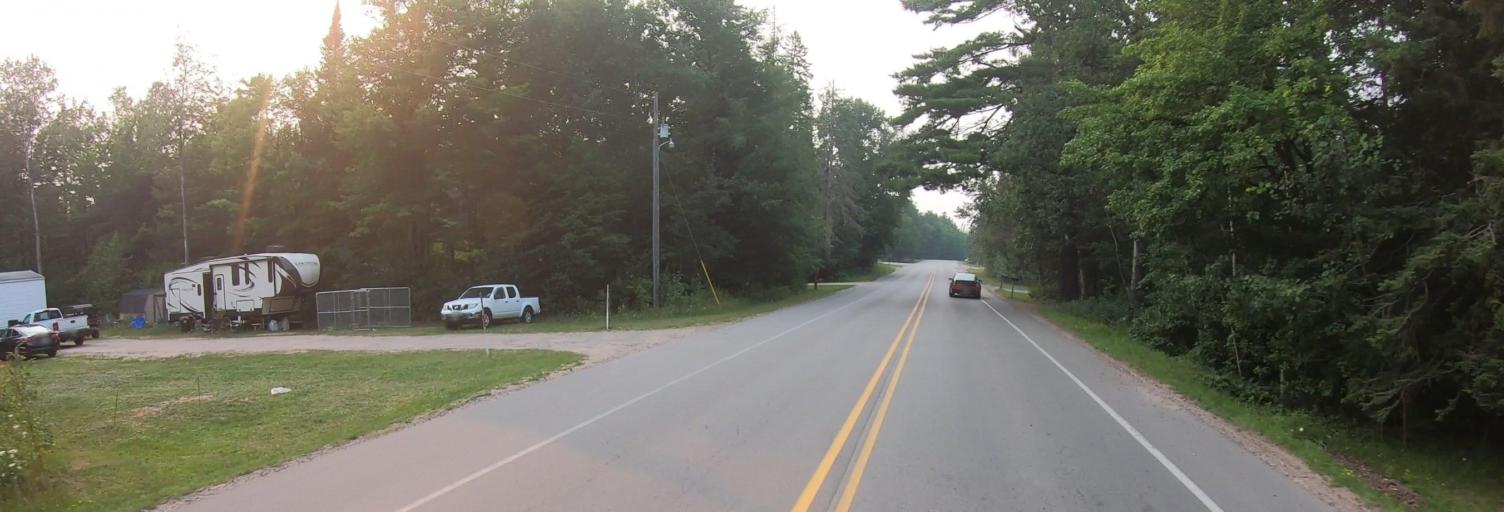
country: US
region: Michigan
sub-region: Chippewa County
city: Sault Ste. Marie
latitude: 46.4555
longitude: -84.6121
